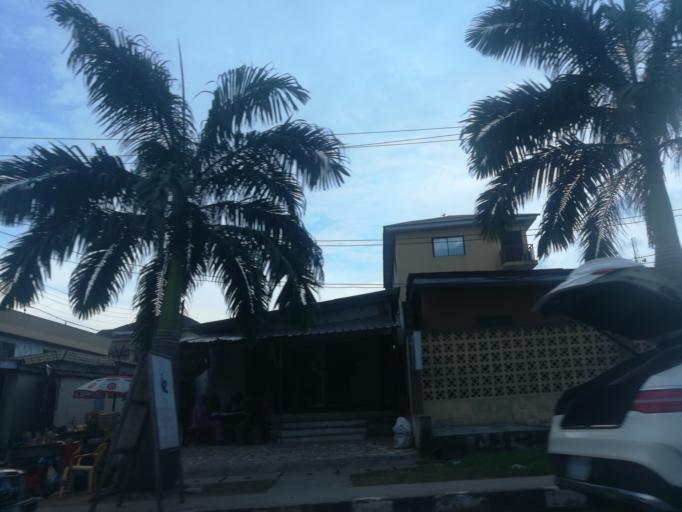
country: NG
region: Lagos
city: Somolu
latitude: 6.5512
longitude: 3.3893
